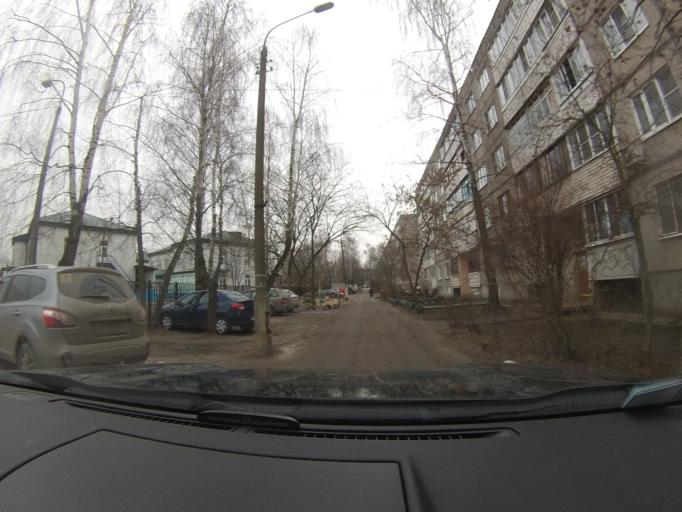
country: RU
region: Moskovskaya
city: Lopatinskiy
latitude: 55.3227
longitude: 38.7005
